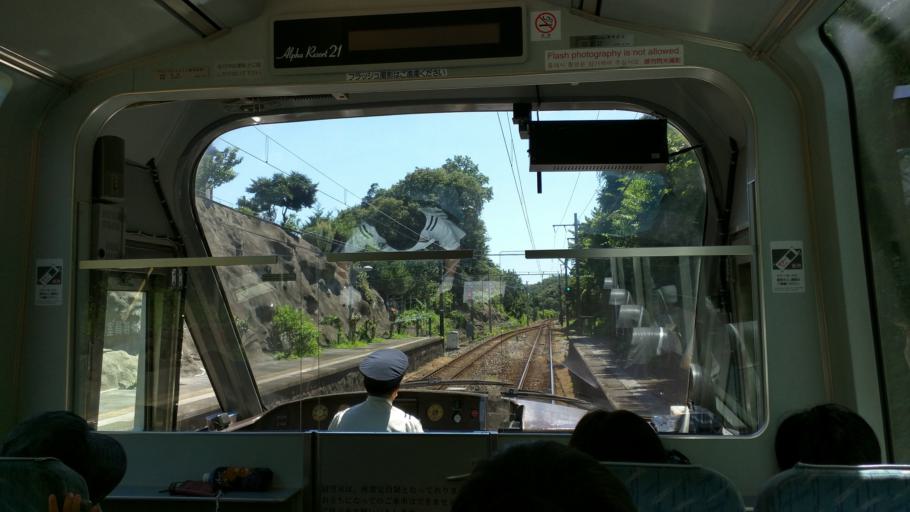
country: JP
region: Shizuoka
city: Ito
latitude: 34.9508
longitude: 139.1257
